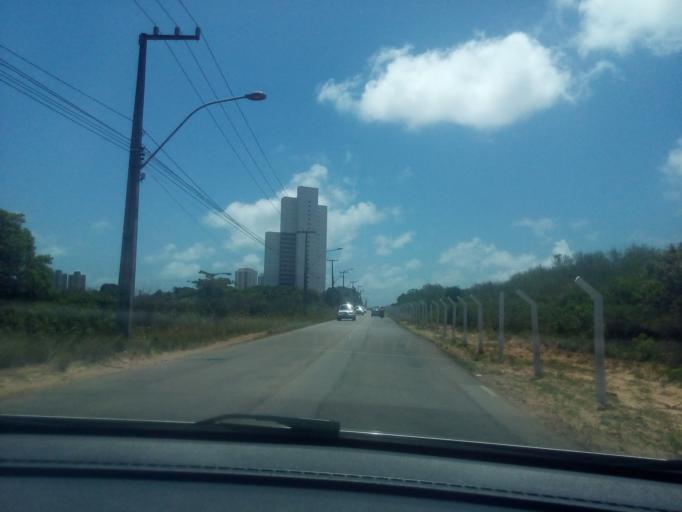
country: BR
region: Rio Grande do Norte
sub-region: Parnamirim
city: Parnamirim
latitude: -5.8887
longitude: -35.1862
